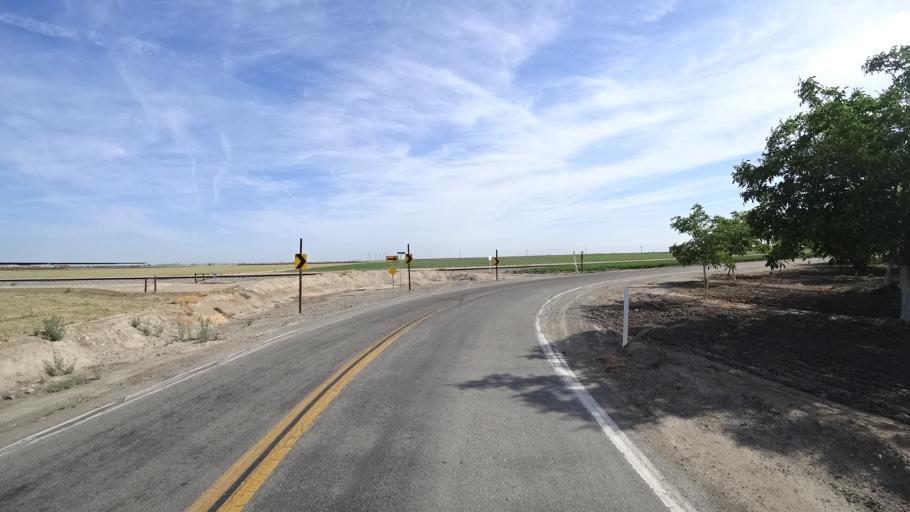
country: US
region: California
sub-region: Tulare County
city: Goshen
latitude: 36.3480
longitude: -119.4930
